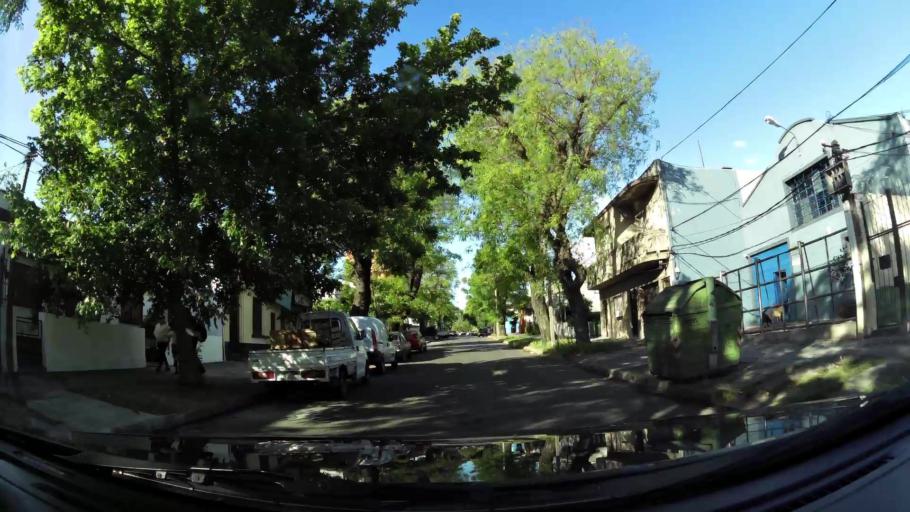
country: UY
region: Montevideo
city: Montevideo
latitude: -34.8766
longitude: -56.1600
